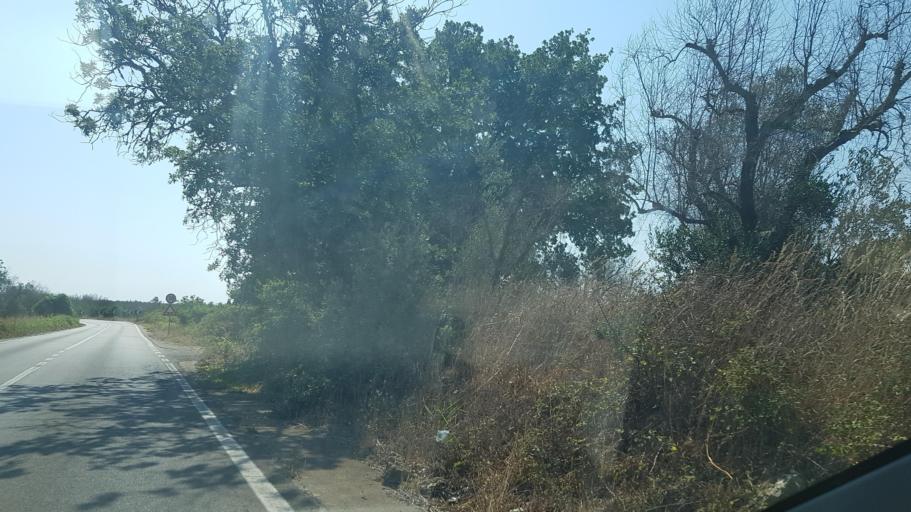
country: IT
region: Apulia
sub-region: Provincia di Lecce
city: Montesano Salentino
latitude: 40.0037
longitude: 18.2998
